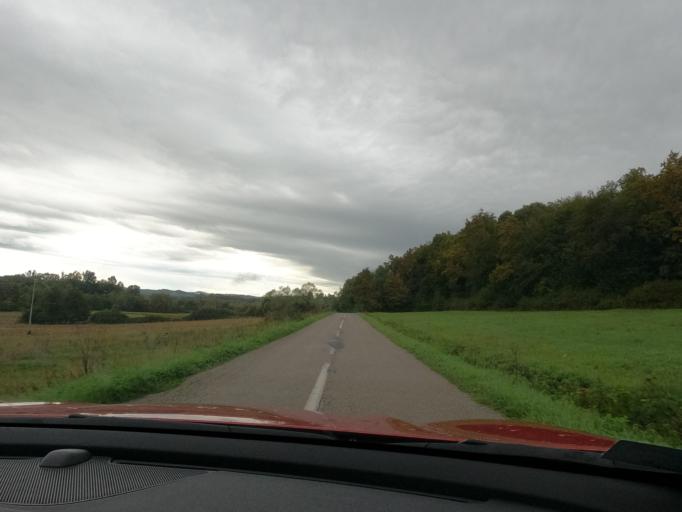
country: HR
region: Sisacko-Moslavacka
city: Glina
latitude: 45.3065
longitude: 16.1797
